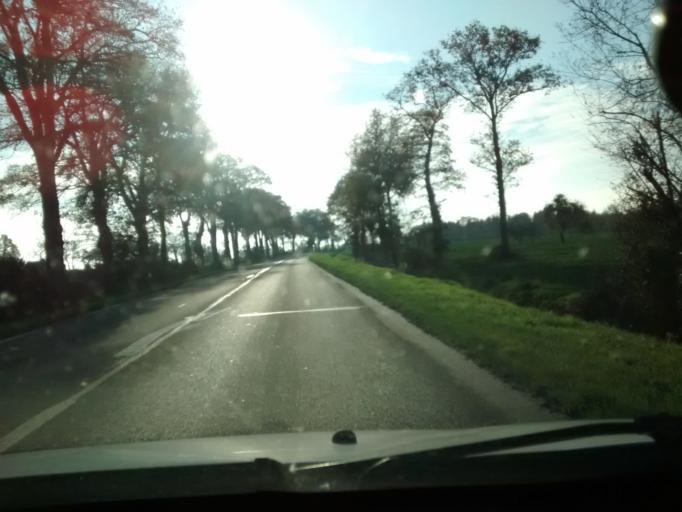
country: FR
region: Brittany
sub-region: Departement d'Ille-et-Vilaine
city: Sens-de-Bretagne
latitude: 48.3082
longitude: -1.5417
